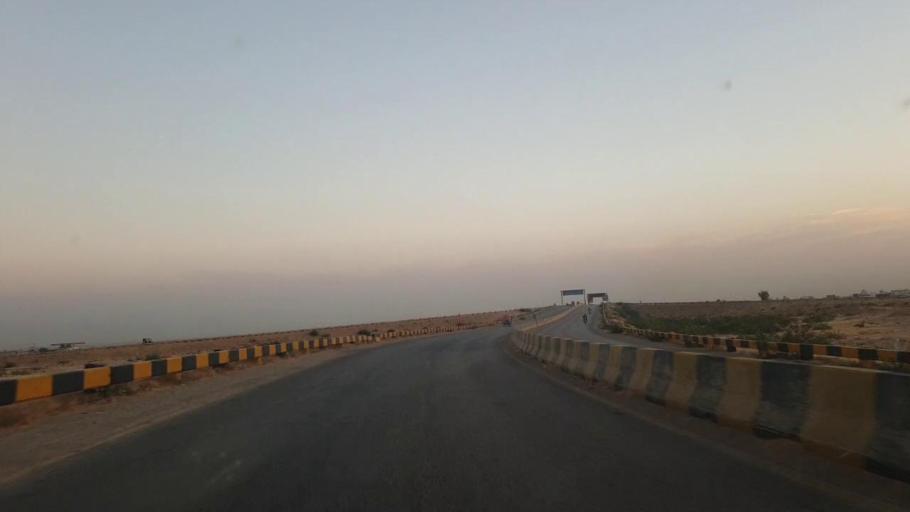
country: PK
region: Sindh
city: Jamshoro
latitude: 25.4034
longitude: 68.2717
